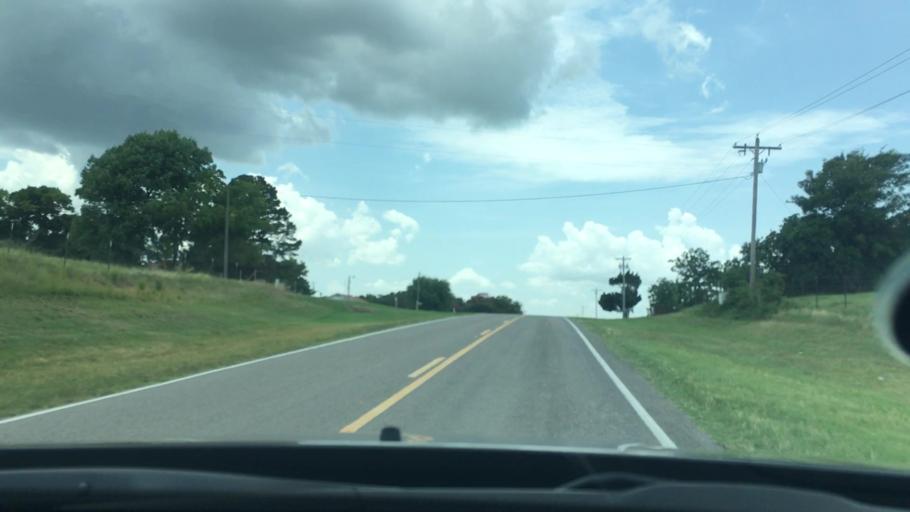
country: US
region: Oklahoma
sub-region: Carter County
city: Wilson
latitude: 33.9403
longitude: -97.3738
